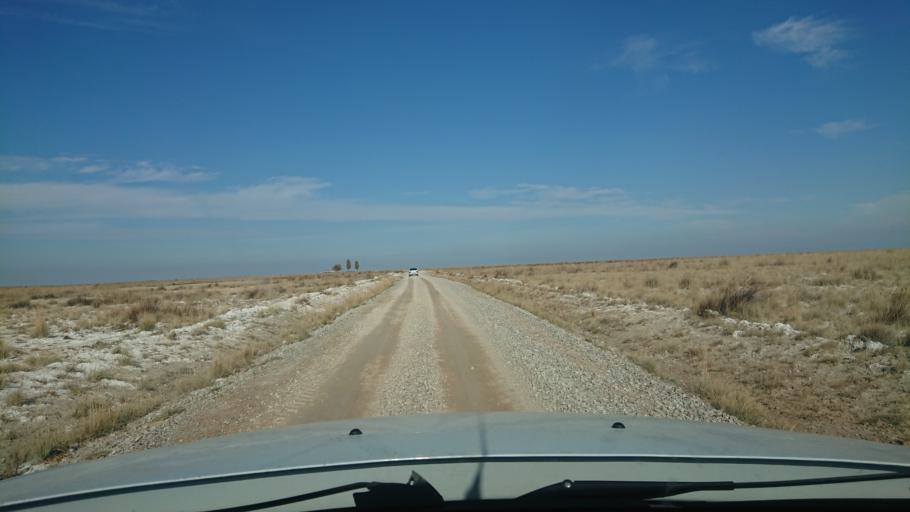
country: TR
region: Aksaray
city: Eskil
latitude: 38.4687
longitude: 33.4558
